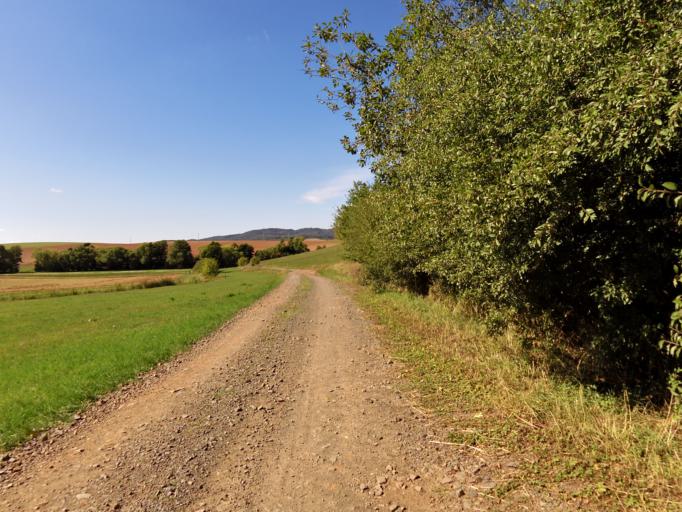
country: DE
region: Rheinland-Pfalz
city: Breunigweiler
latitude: 49.5795
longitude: 7.9750
